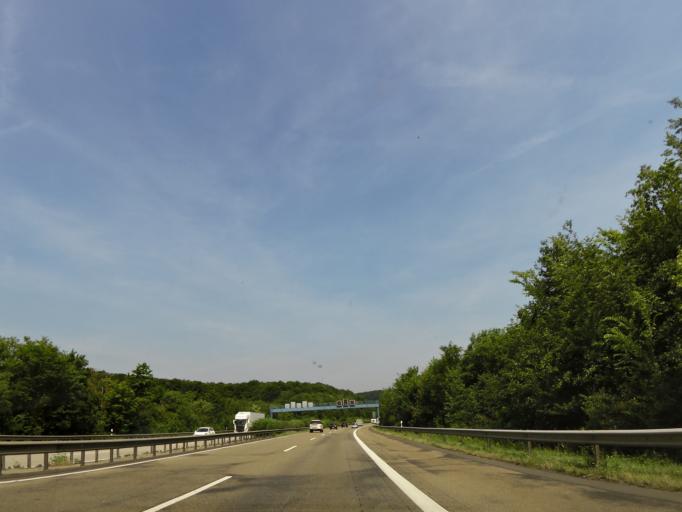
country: DE
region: Rheinland-Pfalz
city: Waldorf
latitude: 50.4793
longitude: 7.2211
